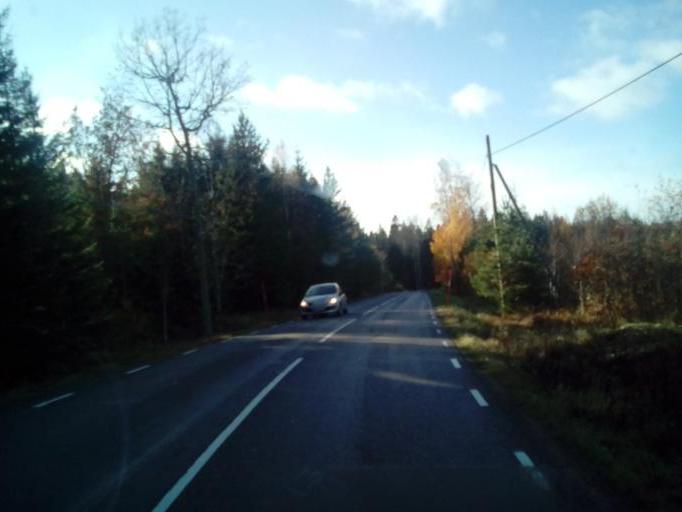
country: SE
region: Kalmar
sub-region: Vasterviks Kommun
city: Ankarsrum
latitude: 57.7390
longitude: 16.1078
